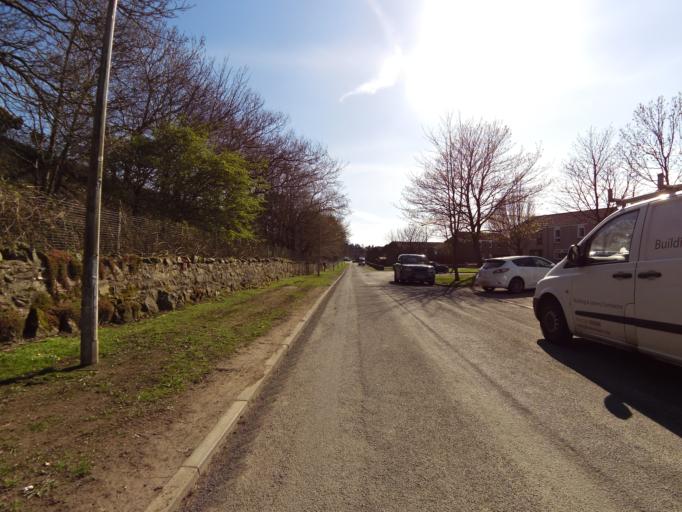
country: GB
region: Scotland
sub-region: Aberdeenshire
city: Portlethen
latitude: 57.0670
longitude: -2.1236
